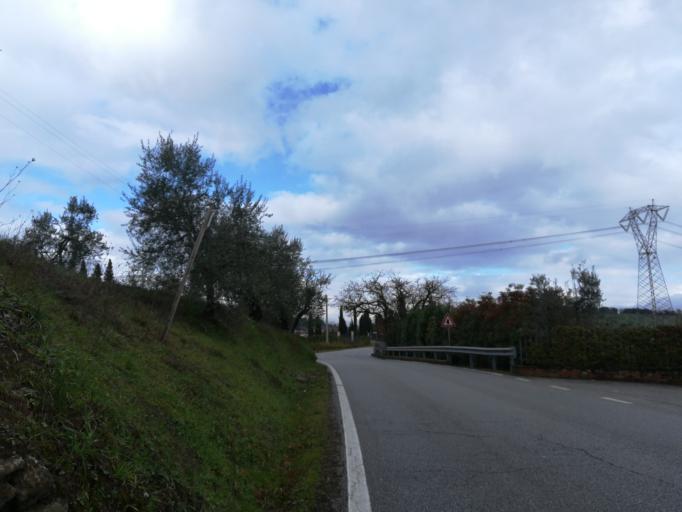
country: IT
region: Tuscany
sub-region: Provincia di Prato
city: Carmignano
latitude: 43.7994
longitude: 11.0315
